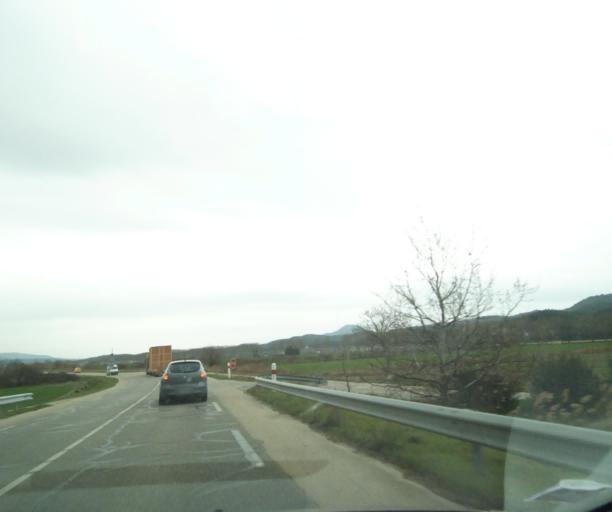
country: FR
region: Provence-Alpes-Cote d'Azur
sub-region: Departement des Bouches-du-Rhone
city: Meyrargues
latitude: 43.6479
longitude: 5.5474
